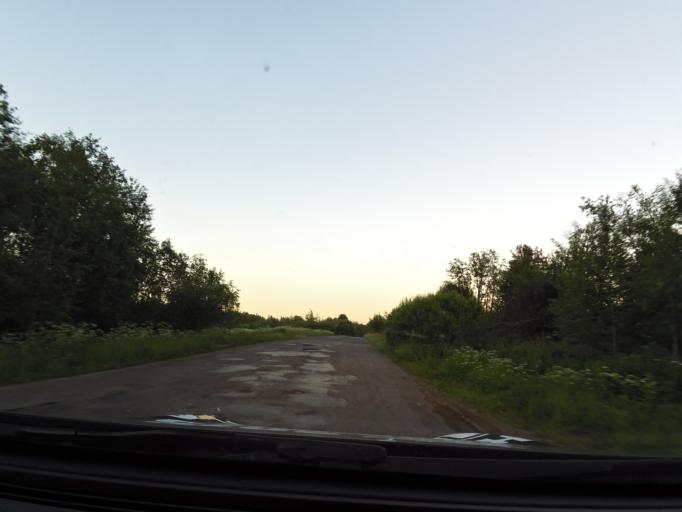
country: RU
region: Leningrad
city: Voznesen'ye
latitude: 60.8484
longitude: 35.5929
